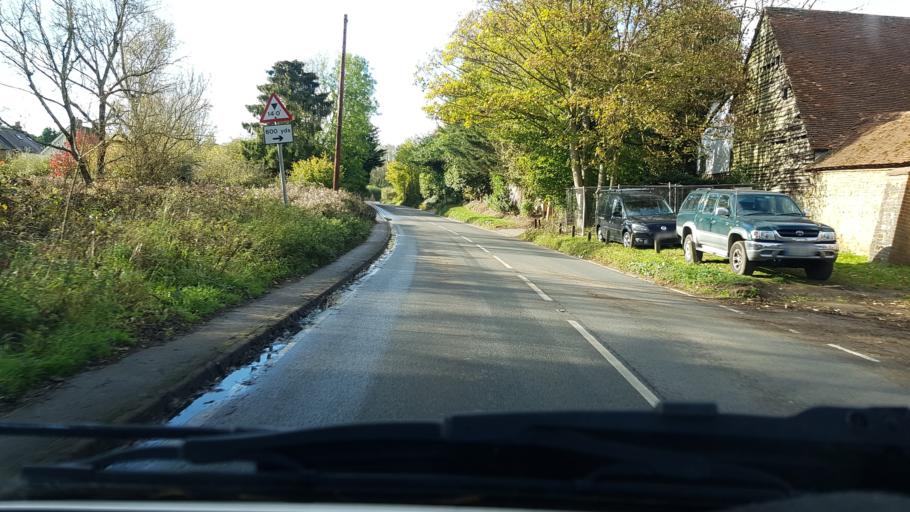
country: GB
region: England
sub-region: Surrey
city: East Horsley
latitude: 51.2173
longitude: -0.4356
